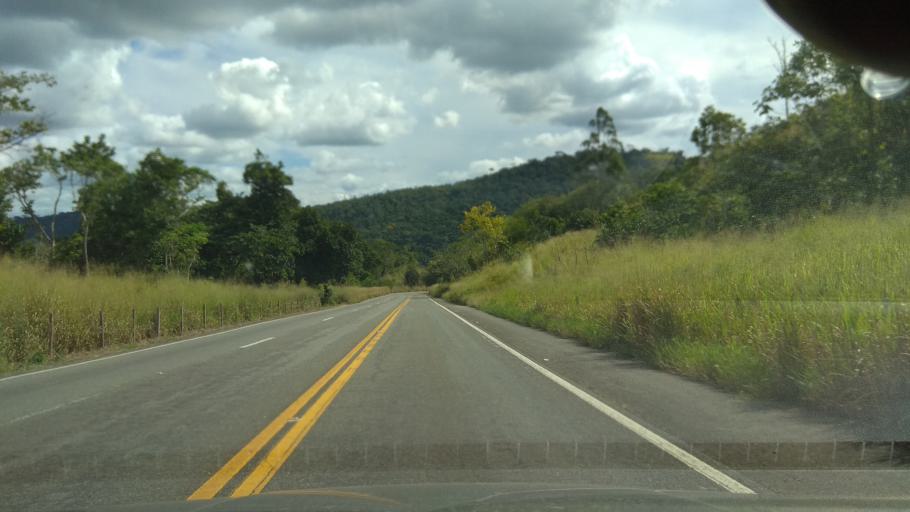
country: BR
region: Bahia
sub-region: Ubaitaba
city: Ubaitaba
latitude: -14.2525
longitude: -39.3713
